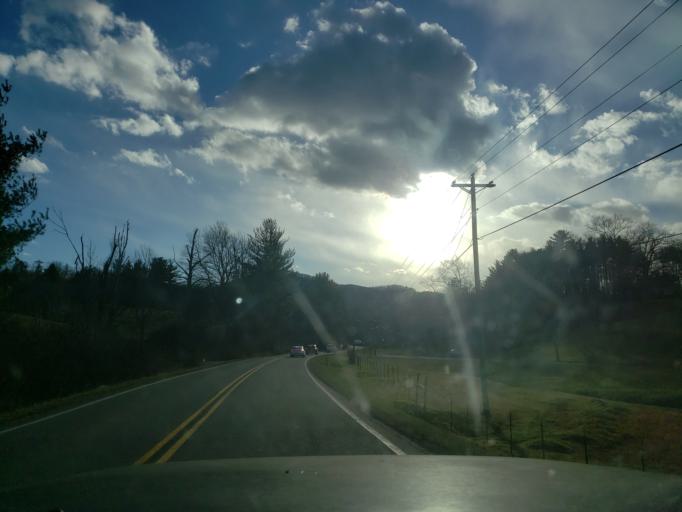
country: US
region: North Carolina
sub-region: Watauga County
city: Boone
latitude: 36.2031
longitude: -81.6357
